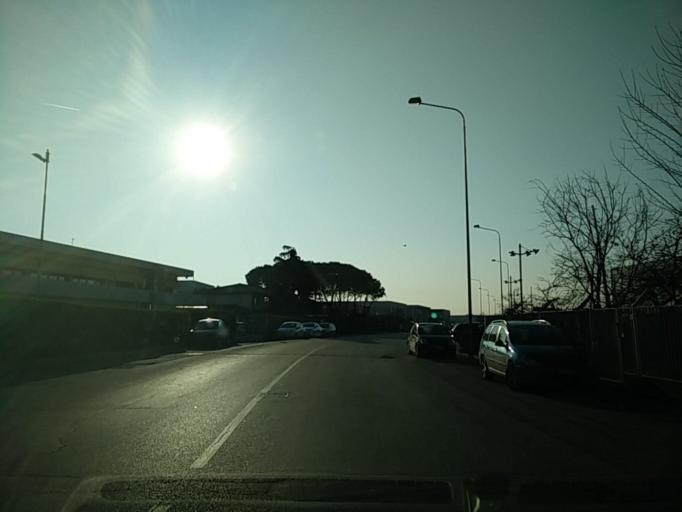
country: IT
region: Veneto
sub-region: Provincia di Venezia
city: San Dona di Piave
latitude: 45.6251
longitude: 12.5949
